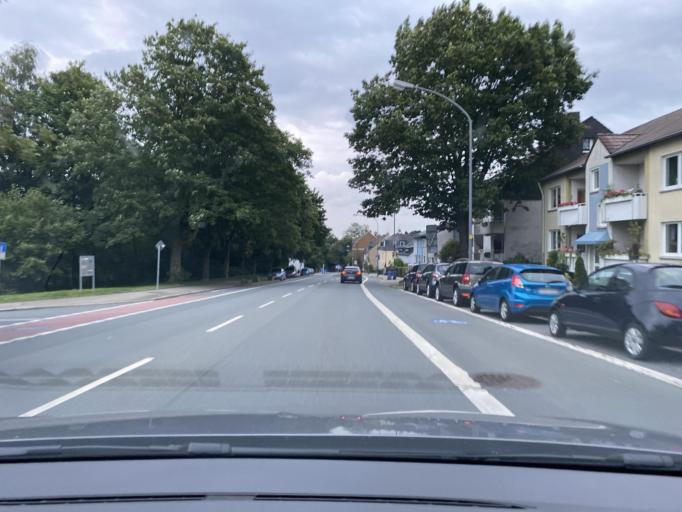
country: DE
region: North Rhine-Westphalia
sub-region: Regierungsbezirk Dusseldorf
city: Essen
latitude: 51.4343
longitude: 7.0777
